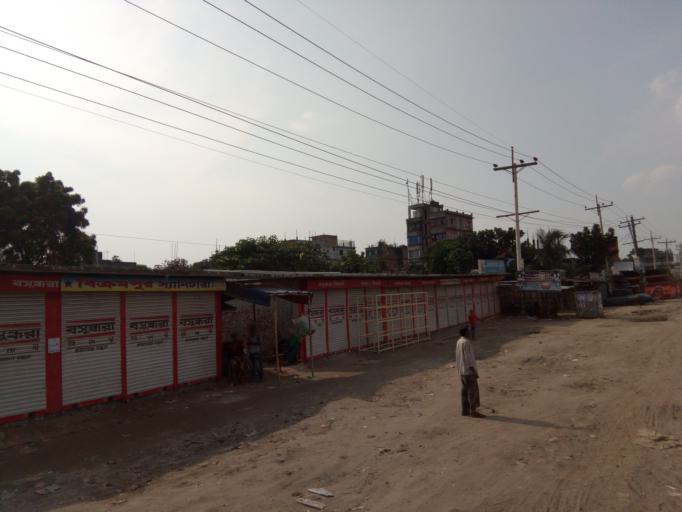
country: BD
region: Dhaka
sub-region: Dhaka
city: Dhaka
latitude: 23.6905
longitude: 90.4004
